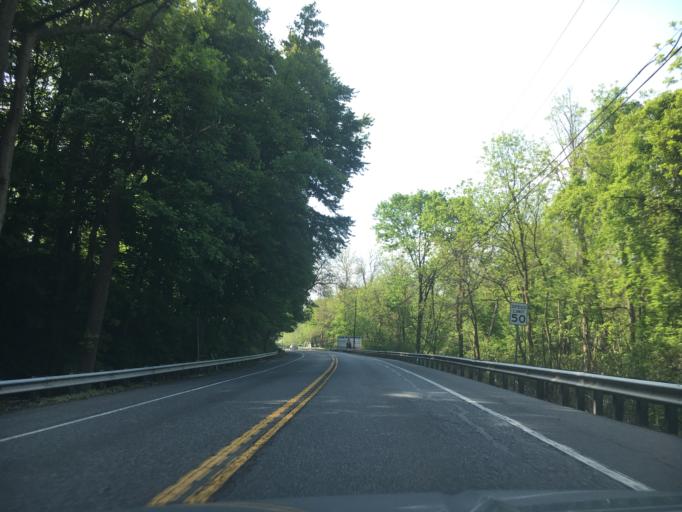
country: US
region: Pennsylvania
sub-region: Berks County
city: New Berlinville
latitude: 40.3568
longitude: -75.6652
